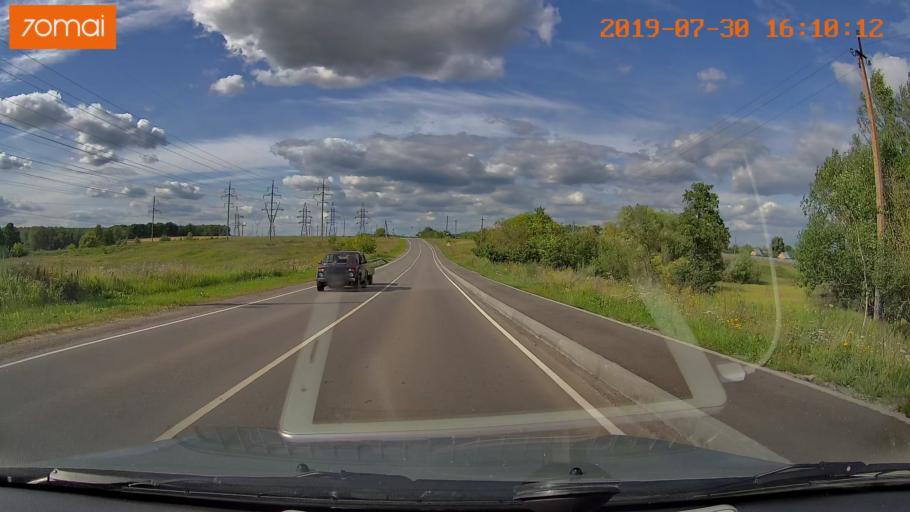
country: RU
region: Moskovskaya
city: Peski
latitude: 55.2602
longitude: 38.7156
